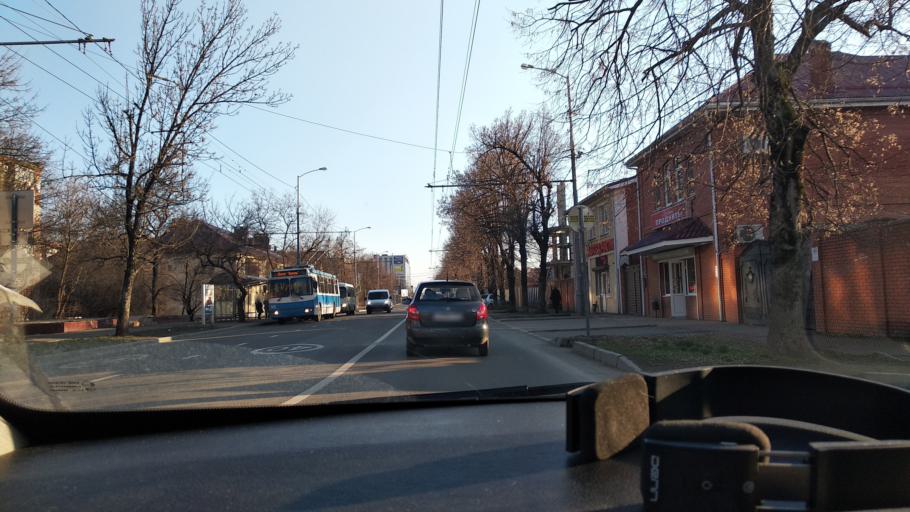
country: RU
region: Adygeya
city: Yablonovskiy
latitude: 45.0074
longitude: 38.9604
